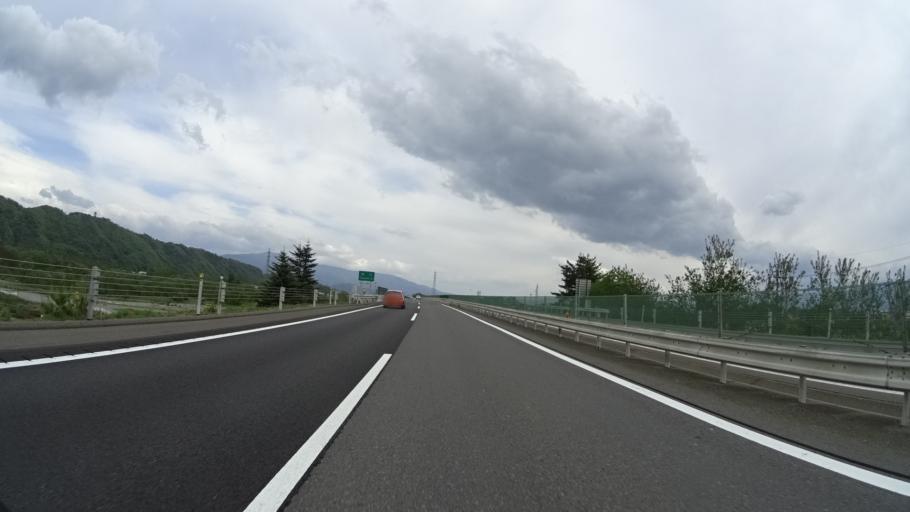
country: JP
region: Nagano
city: Toyoshina
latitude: 36.2664
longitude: 137.9323
